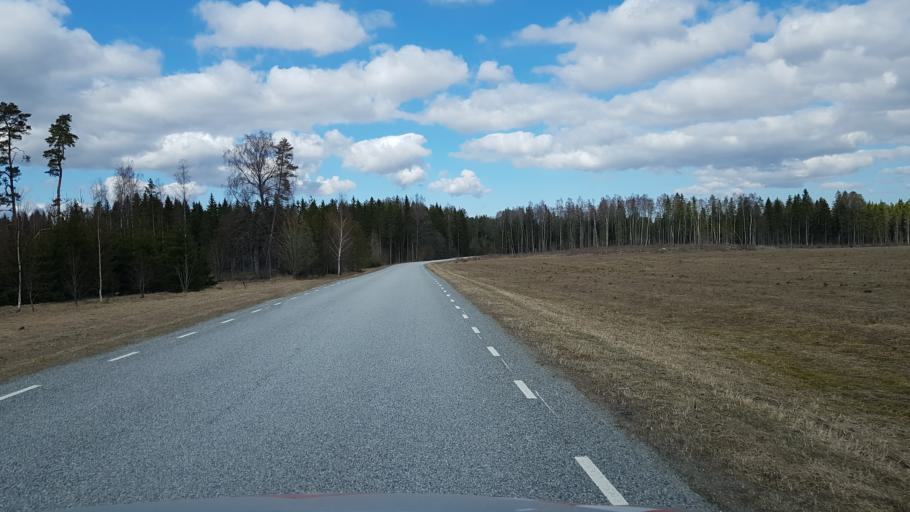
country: EE
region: Laeaene-Virumaa
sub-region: Tamsalu vald
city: Tamsalu
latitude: 59.2264
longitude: 26.1647
